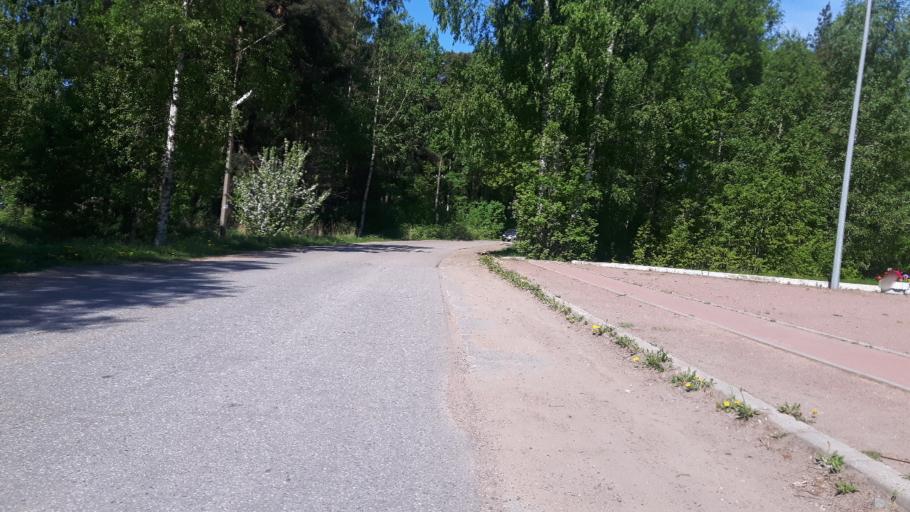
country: RU
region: Leningrad
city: Lebyazh'ye
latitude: 59.9616
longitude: 29.4147
